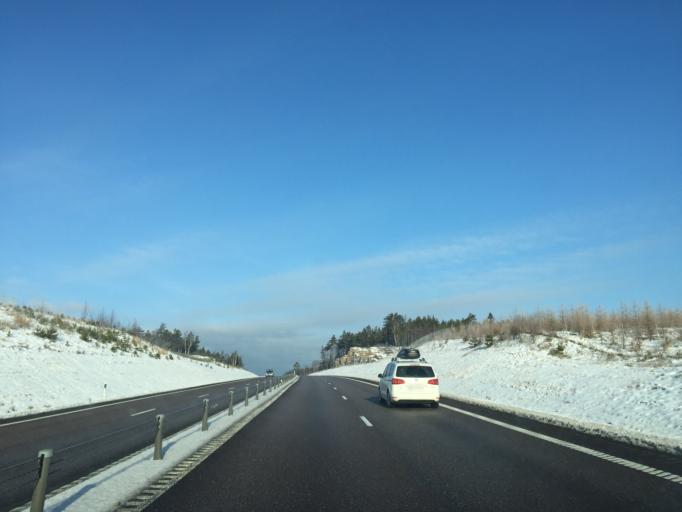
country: SE
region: Vaestra Goetaland
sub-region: Tanums Kommun
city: Tanumshede
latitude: 58.7398
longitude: 11.3032
